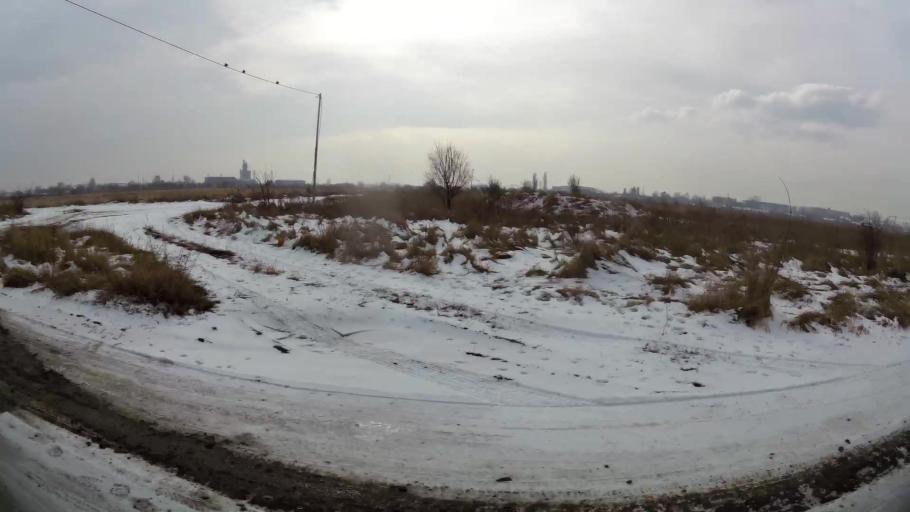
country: BG
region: Sofia-Capital
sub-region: Stolichna Obshtina
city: Sofia
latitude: 42.7057
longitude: 23.4130
